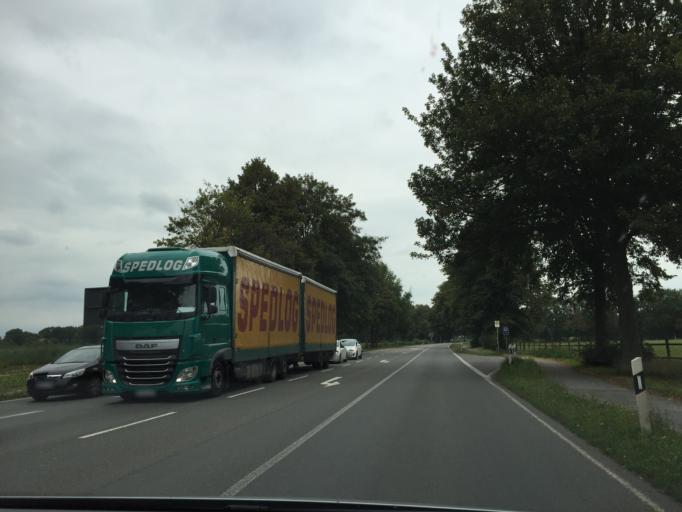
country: DE
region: North Rhine-Westphalia
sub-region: Regierungsbezirk Dusseldorf
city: Voerde
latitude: 51.6304
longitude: 6.7095
